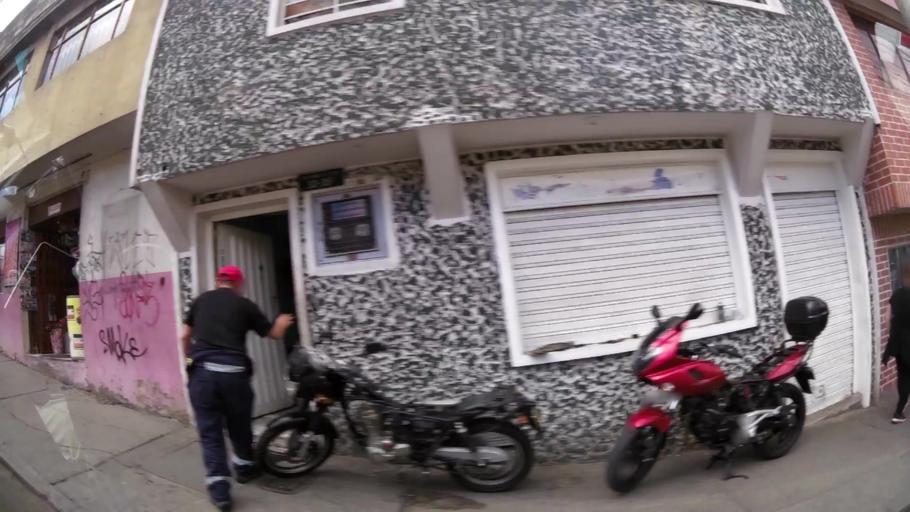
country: CO
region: Bogota D.C.
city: Bogota
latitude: 4.5579
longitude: -74.0910
